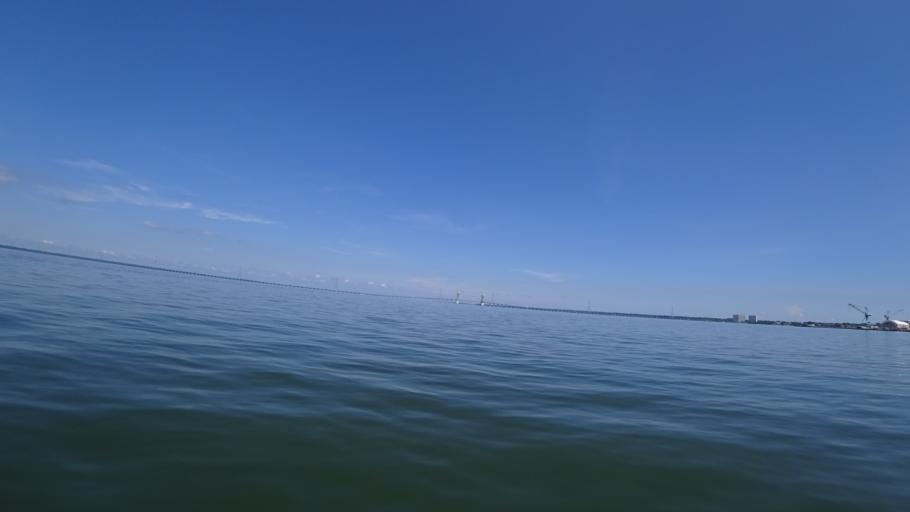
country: US
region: Virginia
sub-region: City of Newport News
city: Newport News
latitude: 36.9886
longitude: -76.4548
